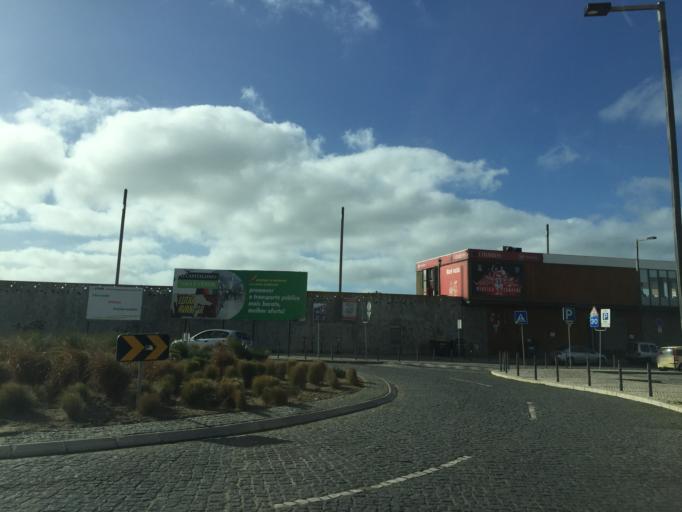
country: PT
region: Setubal
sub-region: Almada
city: Costa de Caparica
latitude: 38.6442
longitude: -9.2402
